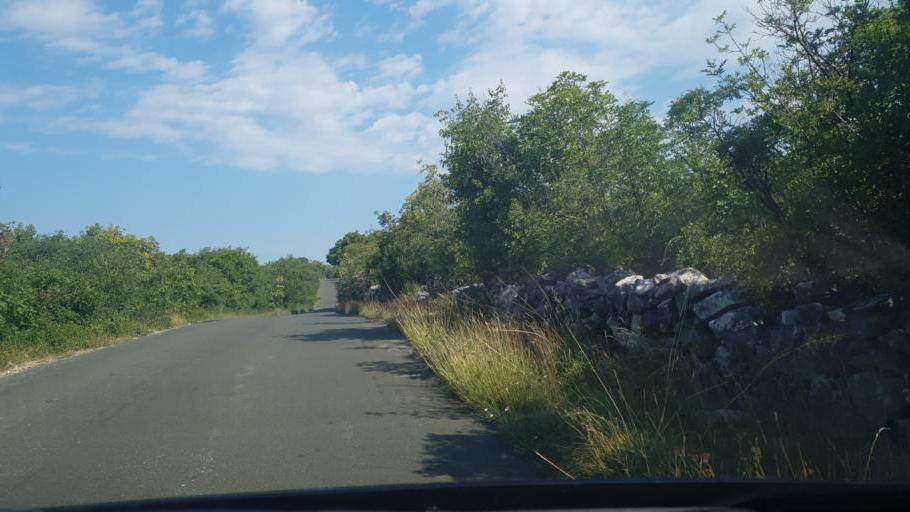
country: HR
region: Primorsko-Goranska
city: Omisalj
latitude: 45.1997
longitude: 14.5735
